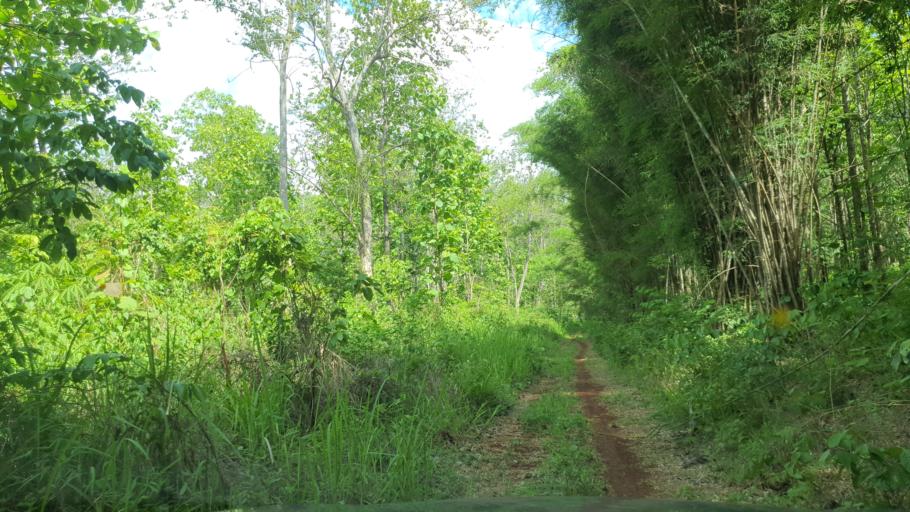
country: TH
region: Chiang Mai
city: Mae Taeng
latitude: 19.0736
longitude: 99.0999
